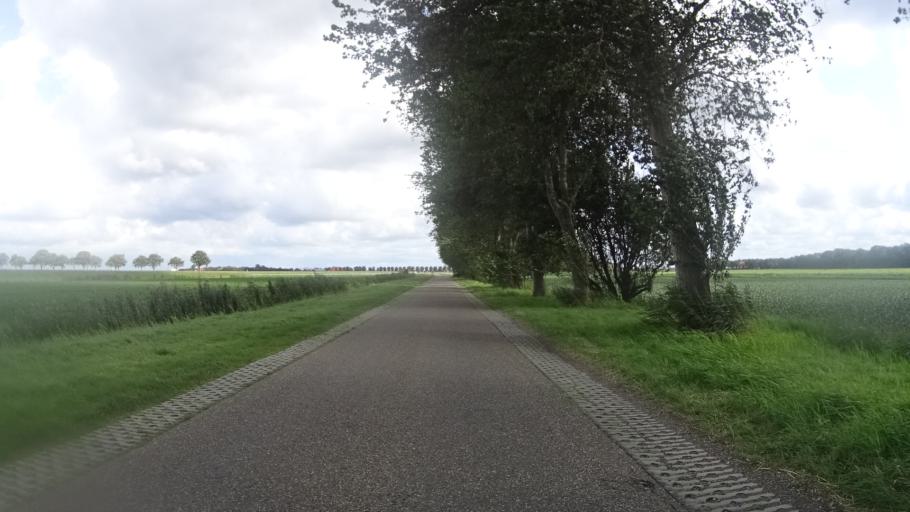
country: NL
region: North Holland
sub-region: Gemeente Hollands Kroon
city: Den Oever
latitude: 52.8834
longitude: 4.9347
